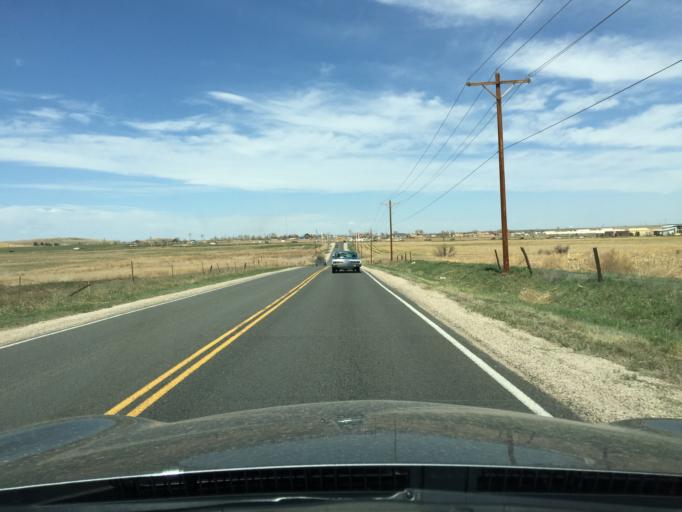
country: US
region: Colorado
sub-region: Boulder County
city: Erie
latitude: 39.9952
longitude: -104.9972
